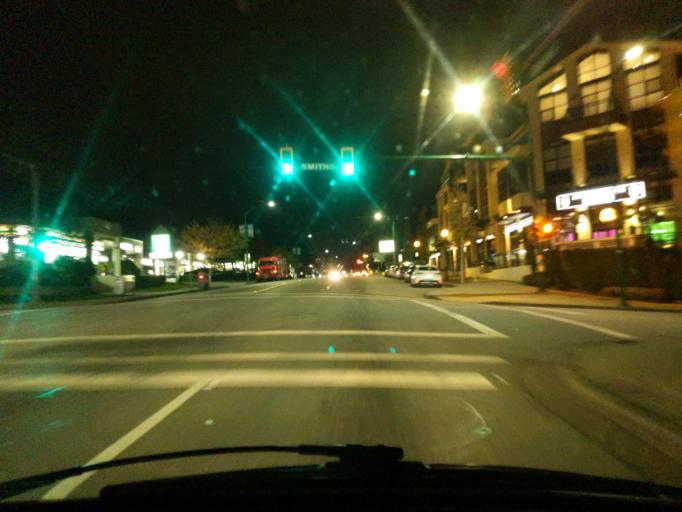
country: CA
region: British Columbia
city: Burnaby
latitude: 49.2547
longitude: -123.0195
